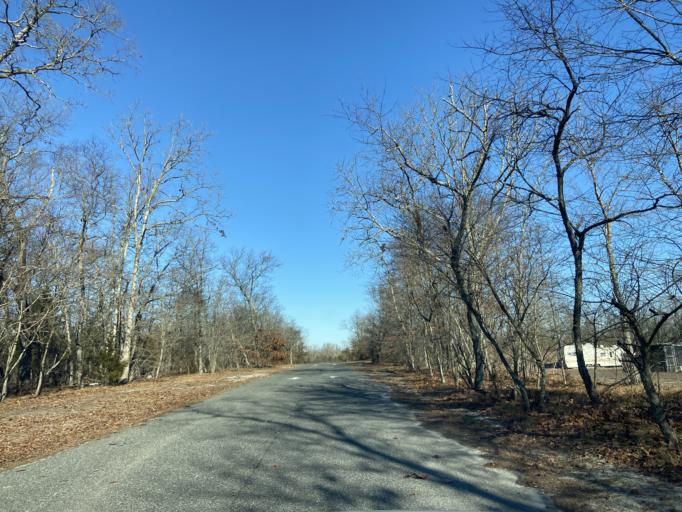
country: US
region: New Jersey
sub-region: Cumberland County
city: Vineland
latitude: 39.4957
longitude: -75.0672
